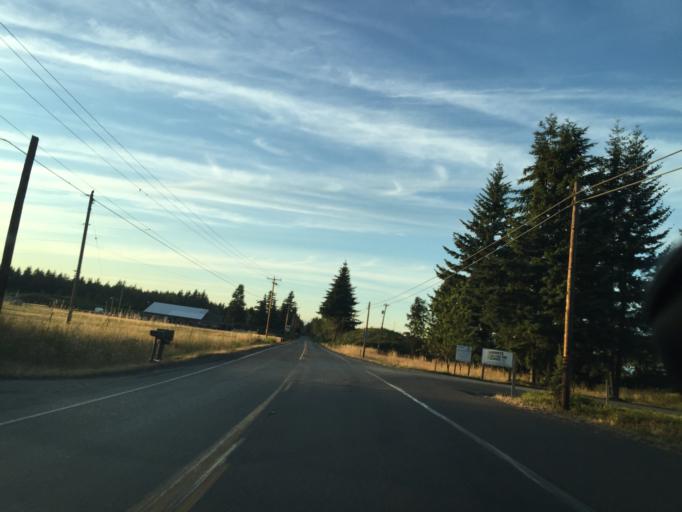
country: US
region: Washington
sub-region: Whatcom County
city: Everson
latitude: 48.8929
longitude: -122.3753
